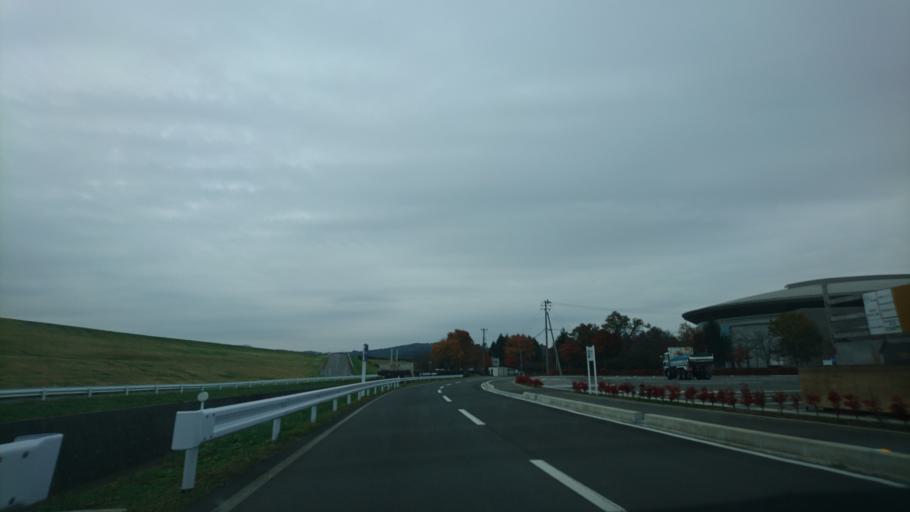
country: JP
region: Iwate
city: Ichinoseki
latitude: 38.9424
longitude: 141.1545
